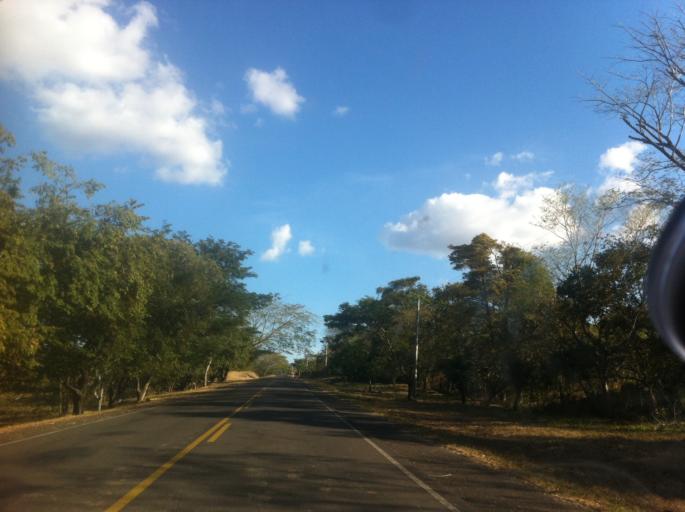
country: NI
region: Chontales
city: Acoyapa
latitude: 11.8783
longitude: -85.0909
